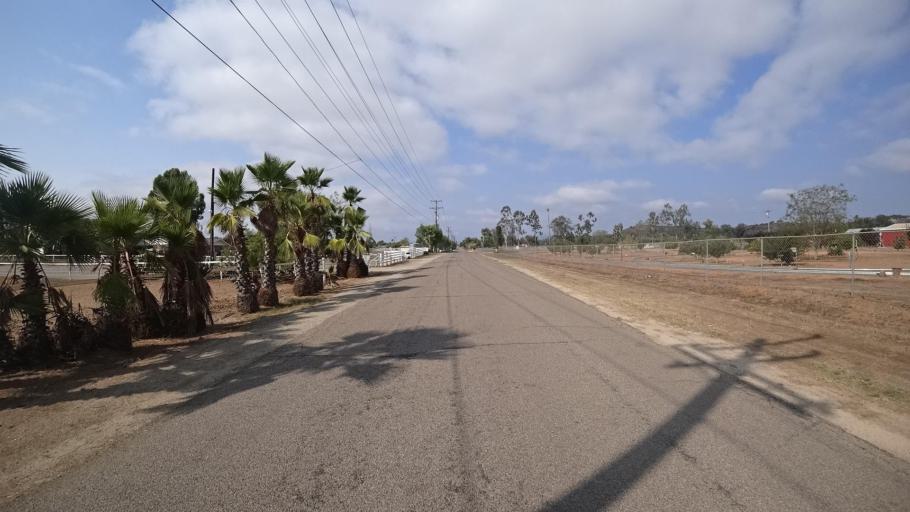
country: US
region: California
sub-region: San Diego County
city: Ramona
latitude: 33.0213
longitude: -116.8493
